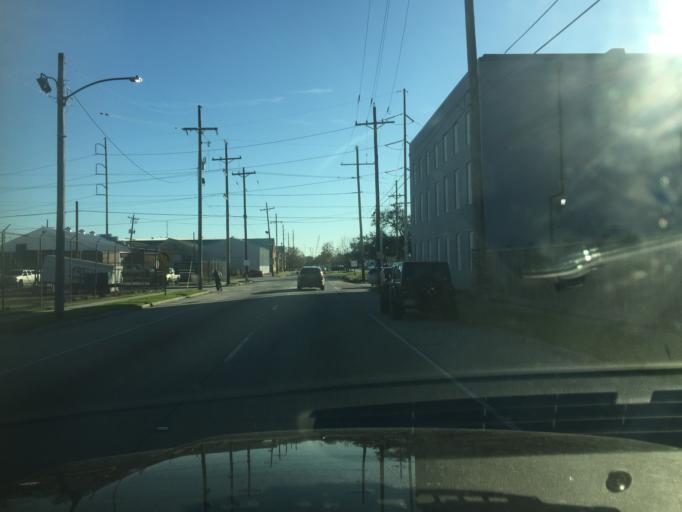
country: US
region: Louisiana
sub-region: Jefferson Parish
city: Gretna
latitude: 29.9287
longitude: -90.0679
